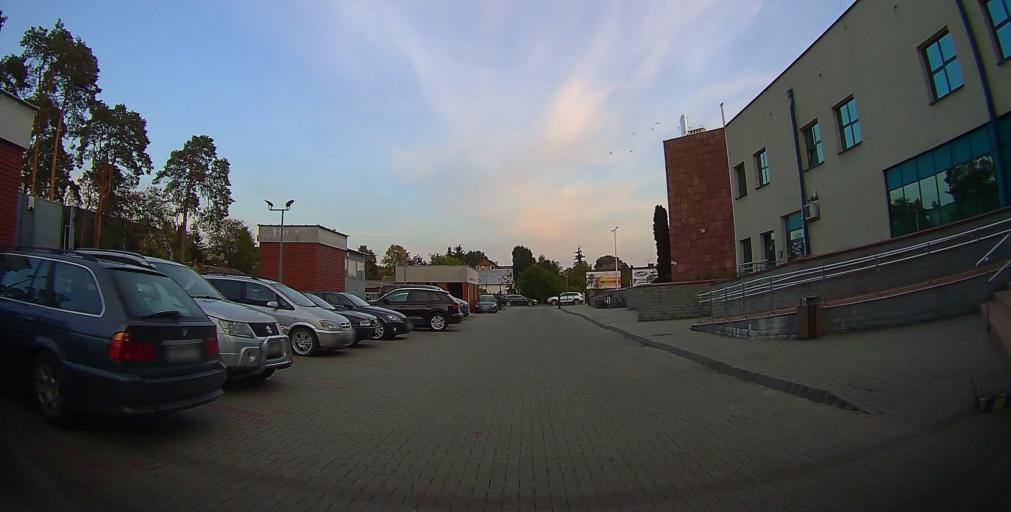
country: PL
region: Masovian Voivodeship
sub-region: Powiat kozienicki
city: Kozienice
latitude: 51.5887
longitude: 21.5427
